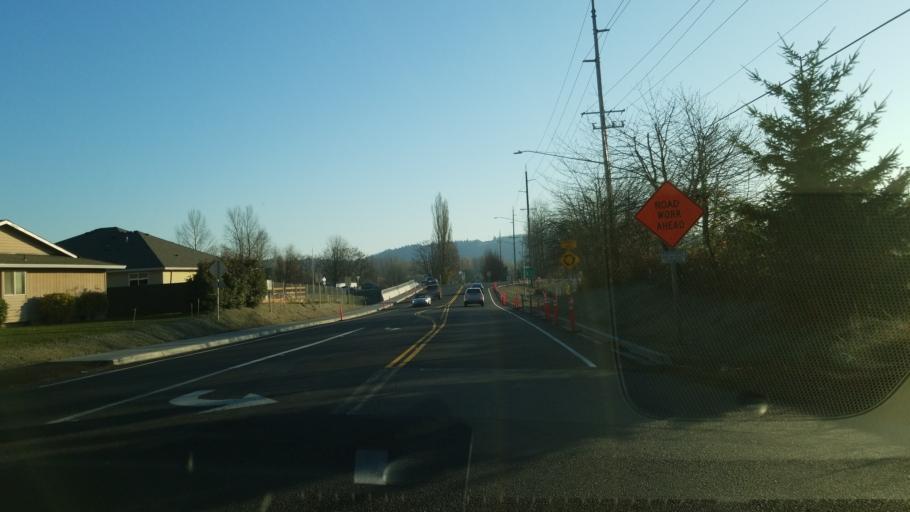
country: US
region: Washington
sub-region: Clark County
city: Washougal
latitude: 45.5760
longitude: -122.3370
